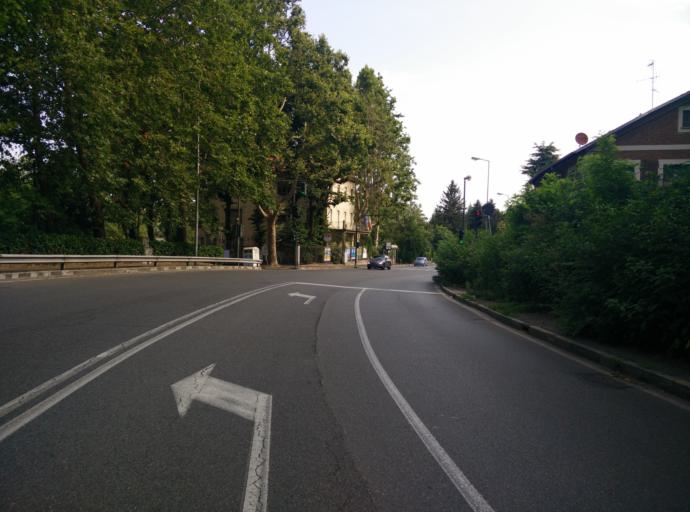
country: IT
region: Piedmont
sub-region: Provincia di Torino
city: Moncalieri
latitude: 45.0246
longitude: 7.6761
